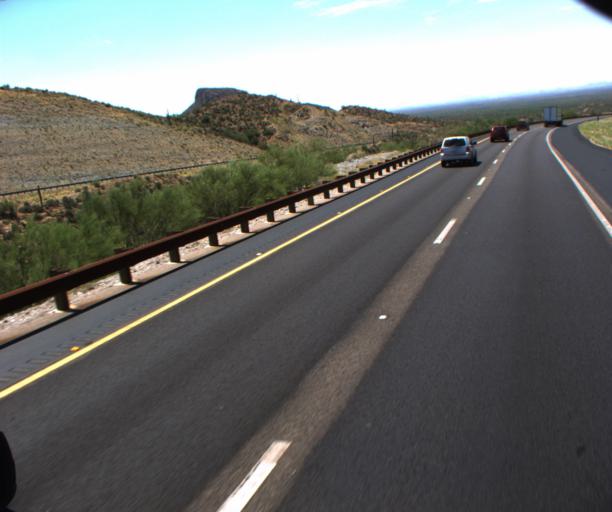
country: US
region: Arizona
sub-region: Pinal County
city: Gold Camp
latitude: 33.2724
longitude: -111.2403
